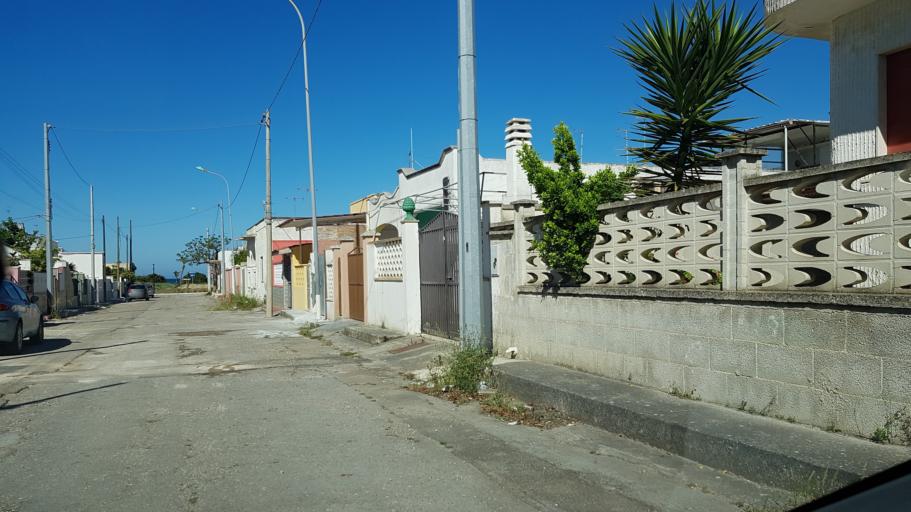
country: IT
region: Apulia
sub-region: Provincia di Brindisi
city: Torchiarolo
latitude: 40.5307
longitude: 18.0765
